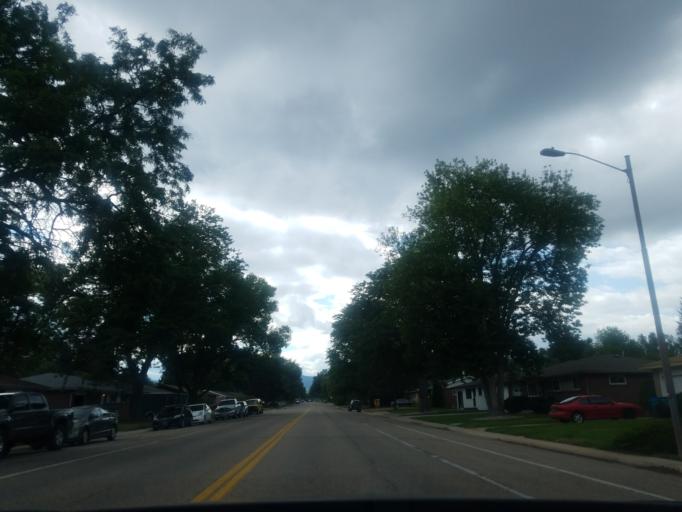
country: US
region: Colorado
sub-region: Larimer County
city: Fort Collins
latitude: 40.5579
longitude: -105.0687
